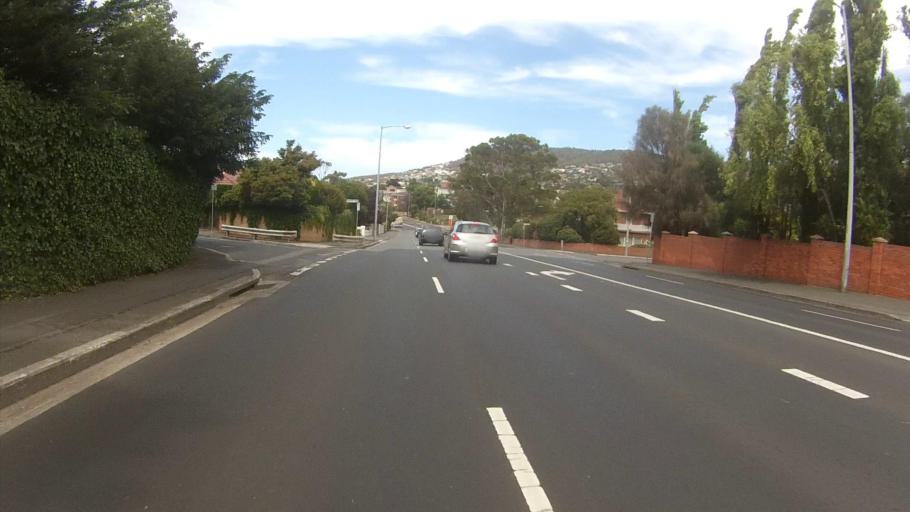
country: AU
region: Tasmania
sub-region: Hobart
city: Sandy Bay
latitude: -42.8985
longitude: 147.3296
